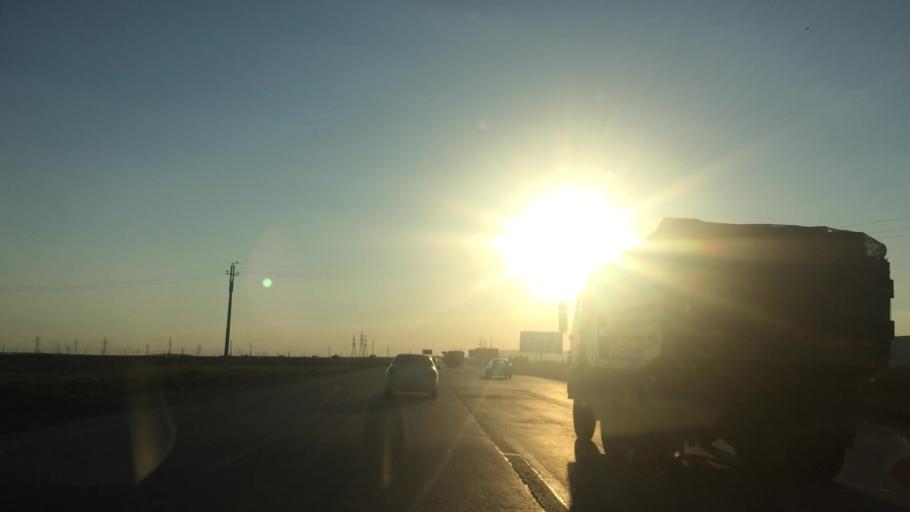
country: AZ
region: Baki
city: Qobustan
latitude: 39.9657
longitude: 49.4059
